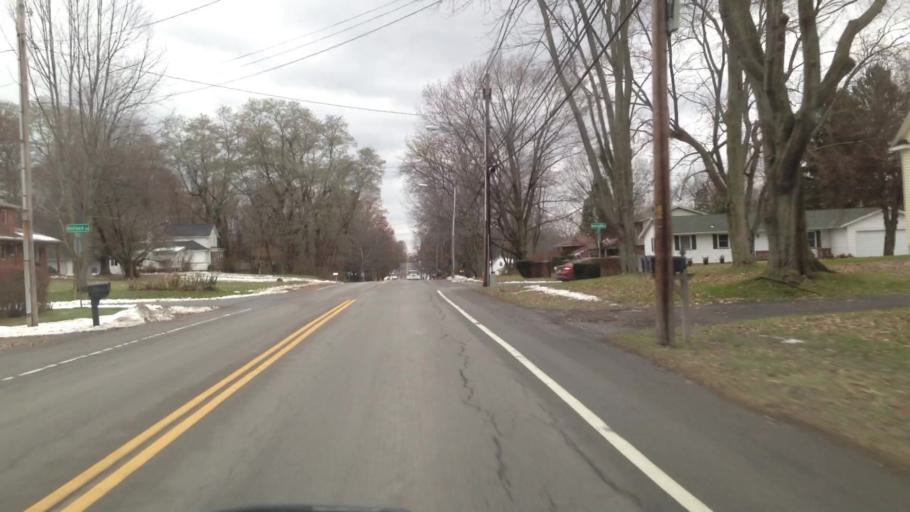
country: US
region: New York
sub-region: Monroe County
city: North Gates
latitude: 43.1256
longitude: -77.7164
